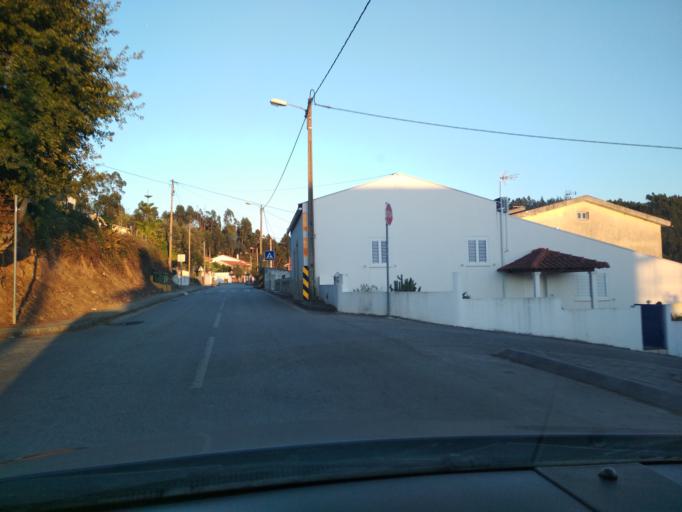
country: PT
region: Coimbra
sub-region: Condeixa-A-Nova
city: Condeixa-a-Nova
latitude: 40.1692
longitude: -8.4780
